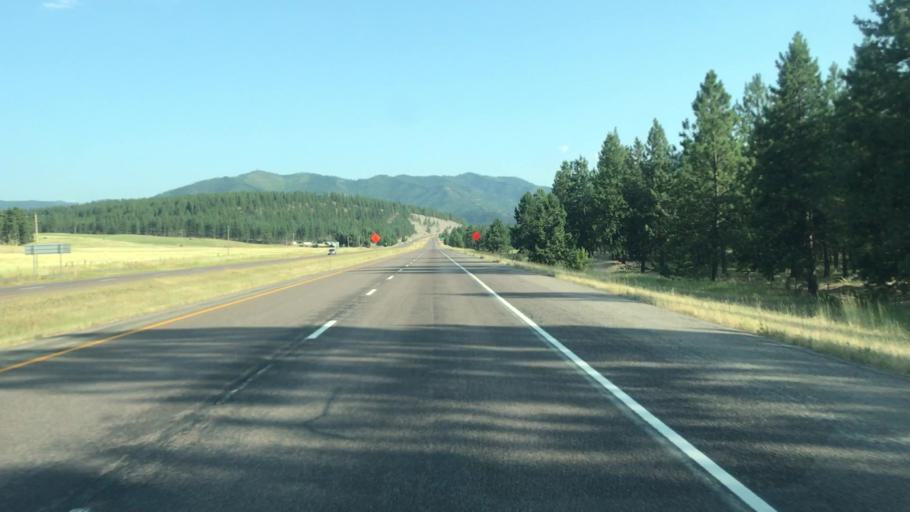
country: US
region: Montana
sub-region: Mineral County
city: Superior
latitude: 47.0356
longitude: -114.7460
